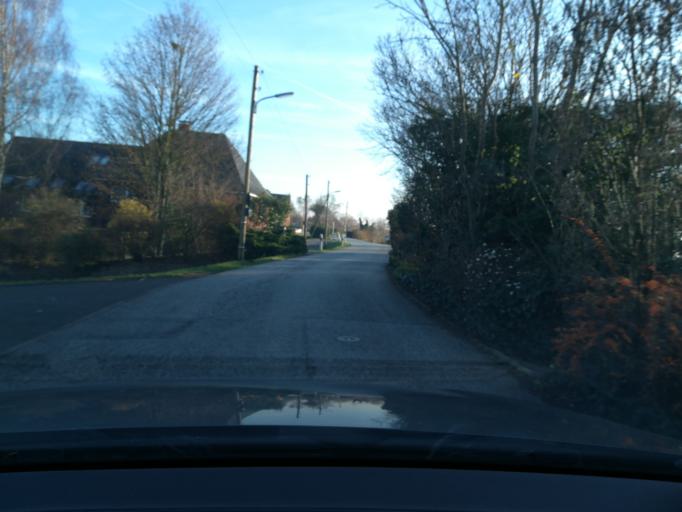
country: DE
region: Lower Saxony
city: Stelle
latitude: 53.4482
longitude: 10.1046
